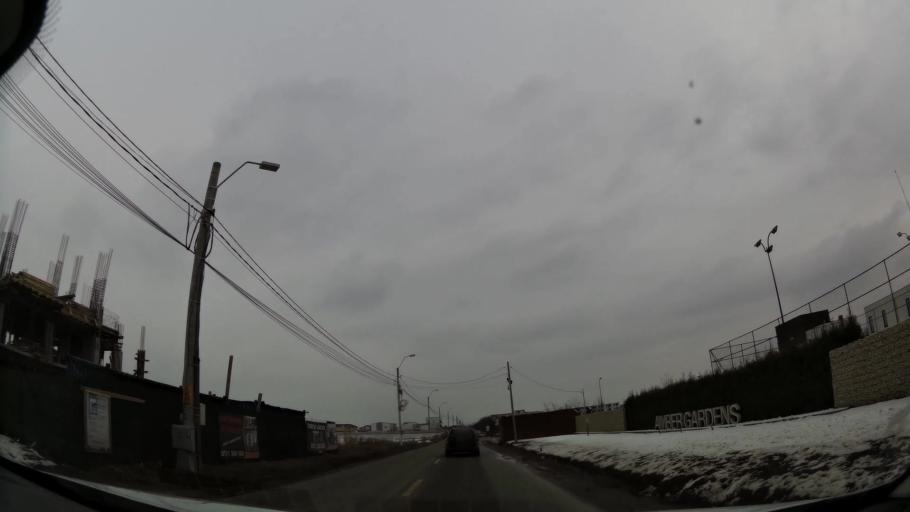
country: RO
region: Ilfov
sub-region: Comuna Tunari
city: Tunari
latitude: 44.5508
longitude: 26.1161
